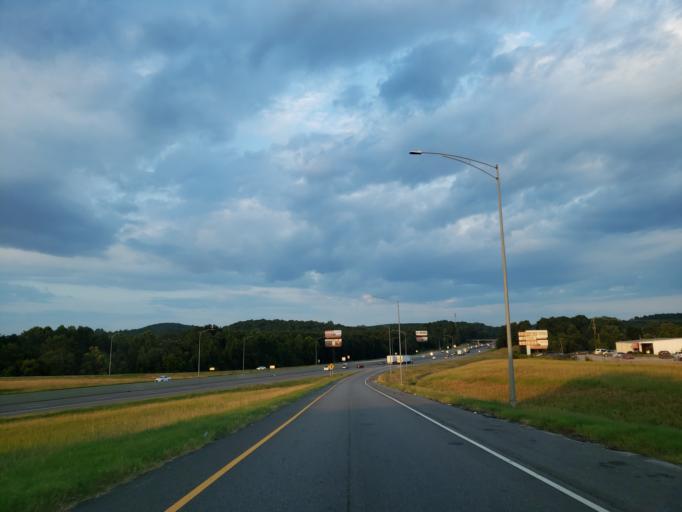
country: US
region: Alabama
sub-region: Tuscaloosa County
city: Holt
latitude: 33.1721
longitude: -87.4464
